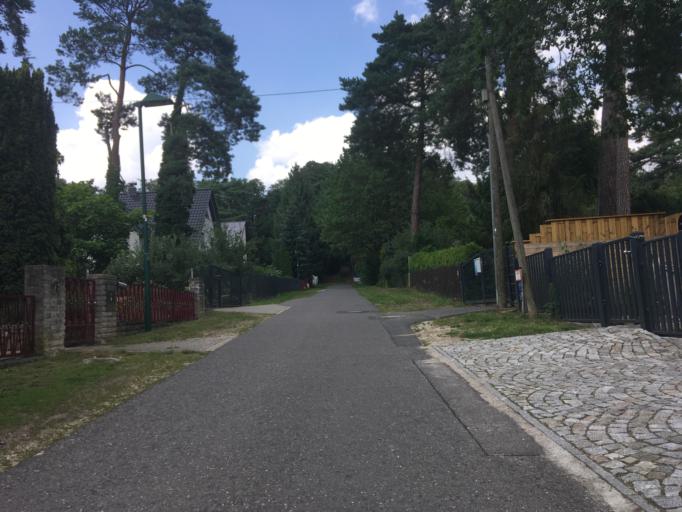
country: DE
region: Brandenburg
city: Wildau
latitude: 52.3297
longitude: 13.6208
